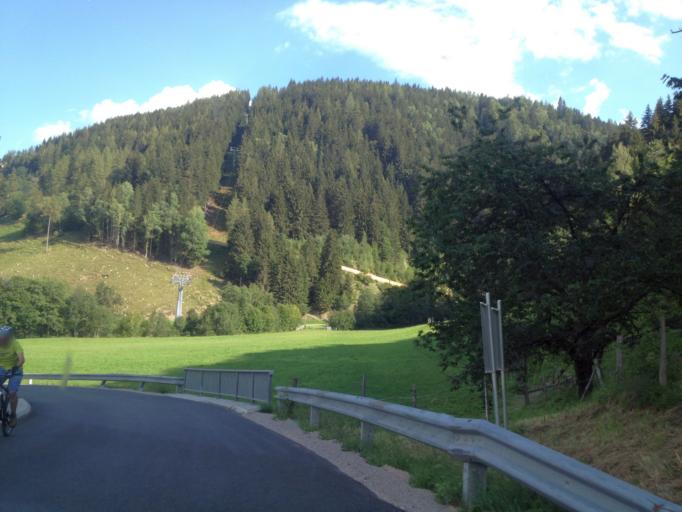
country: AT
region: Styria
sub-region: Politischer Bezirk Liezen
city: Schladming
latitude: 47.3847
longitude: 13.6146
